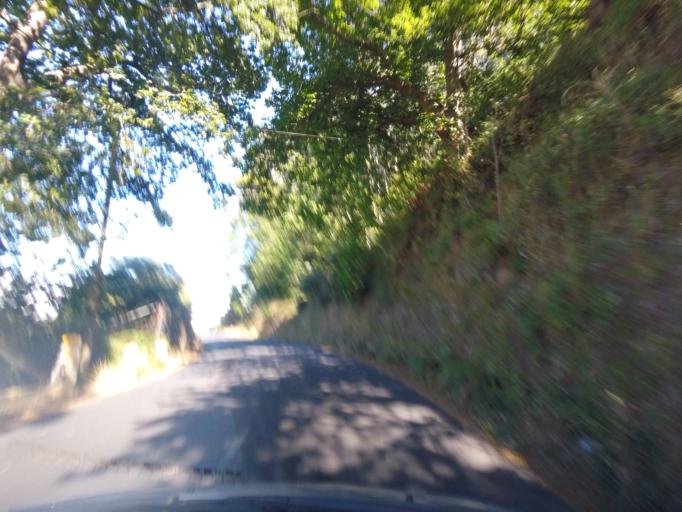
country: PT
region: Madeira
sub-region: Santa Cruz
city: Camacha
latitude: 32.6852
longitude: -16.8507
